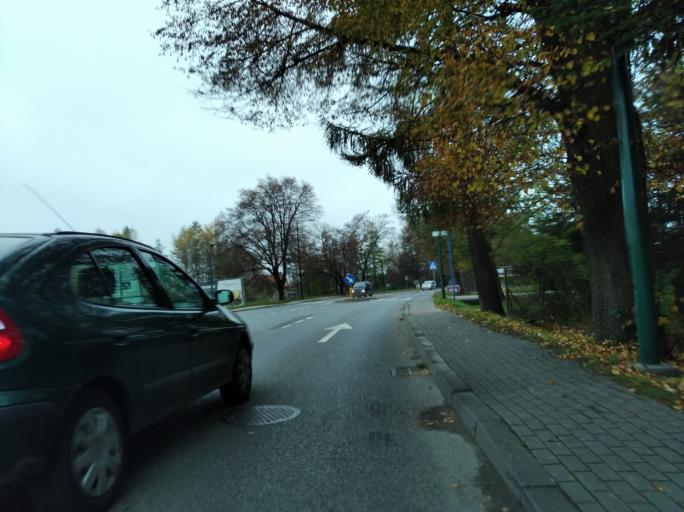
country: PL
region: Subcarpathian Voivodeship
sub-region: Krosno
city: Krosno
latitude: 49.6820
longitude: 21.7225
